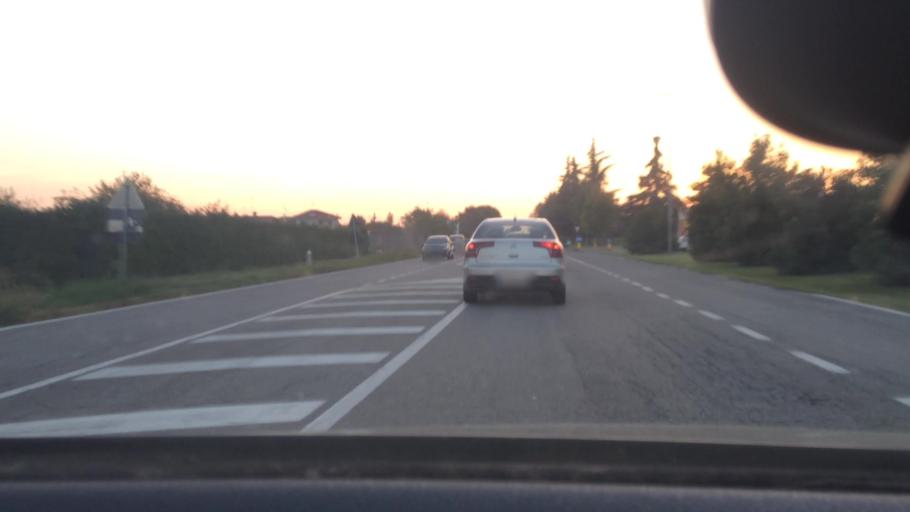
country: IT
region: Lombardy
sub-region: Citta metropolitana di Milano
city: Canegrate
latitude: 45.5463
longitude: 8.9259
